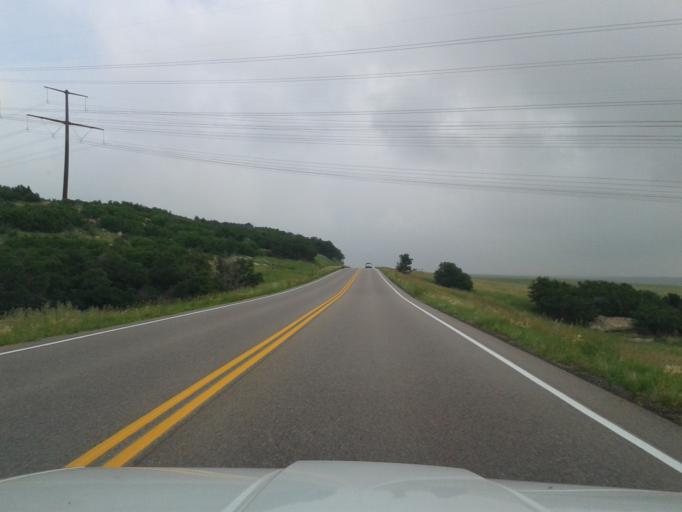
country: US
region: Colorado
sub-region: Douglas County
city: Castle Rock
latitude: 39.2863
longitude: -104.7365
